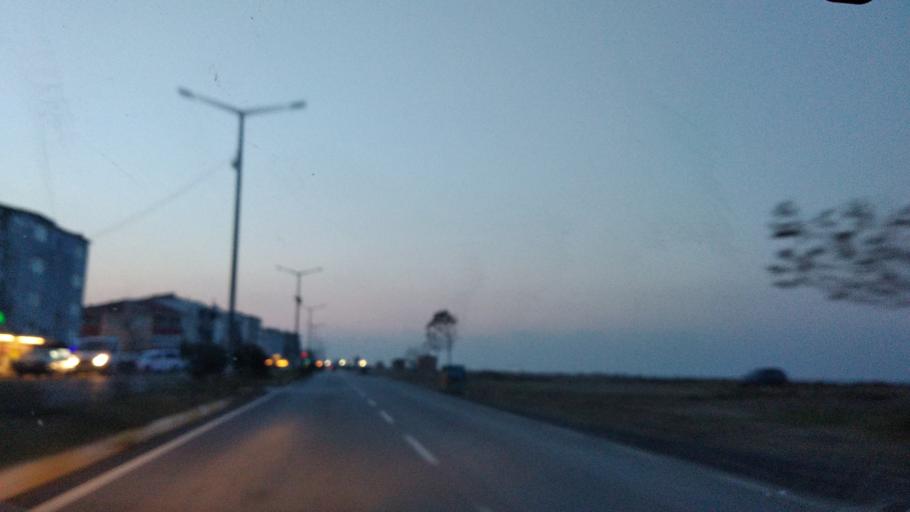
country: TR
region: Sakarya
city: Karasu
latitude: 41.1003
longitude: 30.7197
